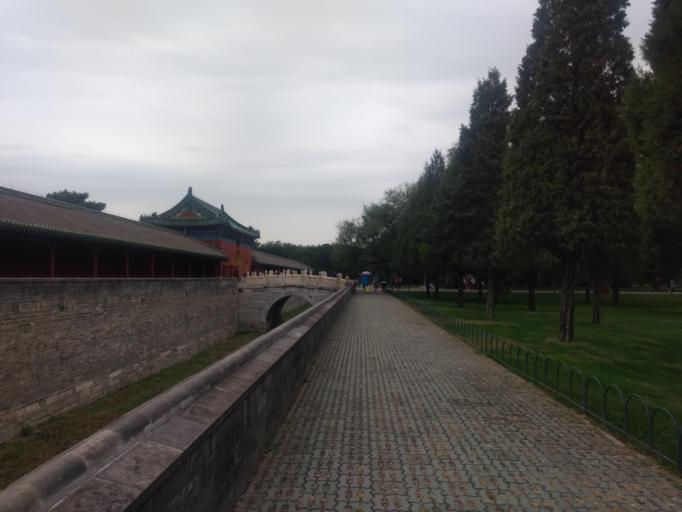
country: CN
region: Beijing
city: Longtan
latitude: 39.8779
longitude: 116.4019
